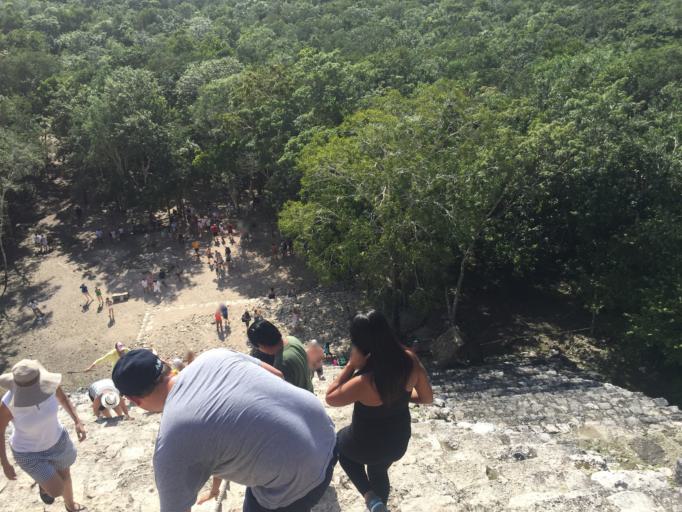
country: MX
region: Quintana Roo
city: Coba
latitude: 20.4947
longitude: -87.7203
